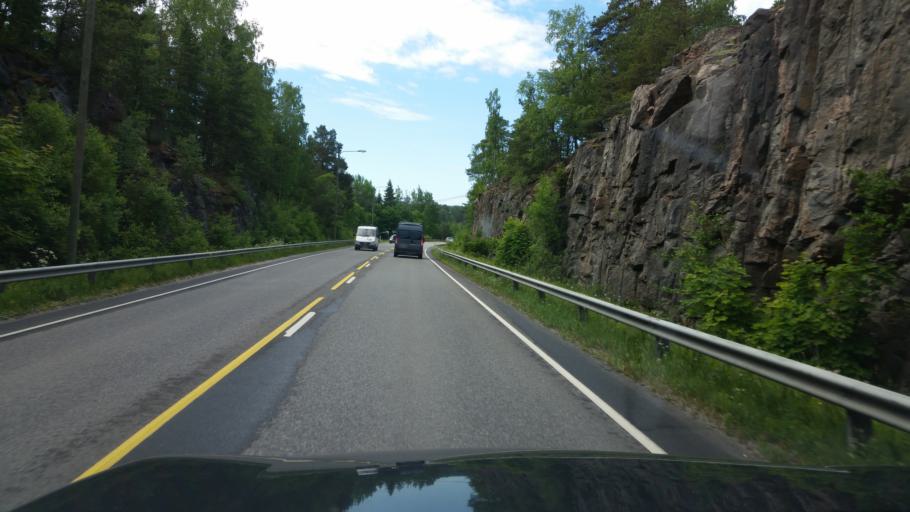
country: FI
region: Varsinais-Suomi
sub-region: Aboland-Turunmaa
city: Pargas
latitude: 60.3265
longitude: 22.3473
